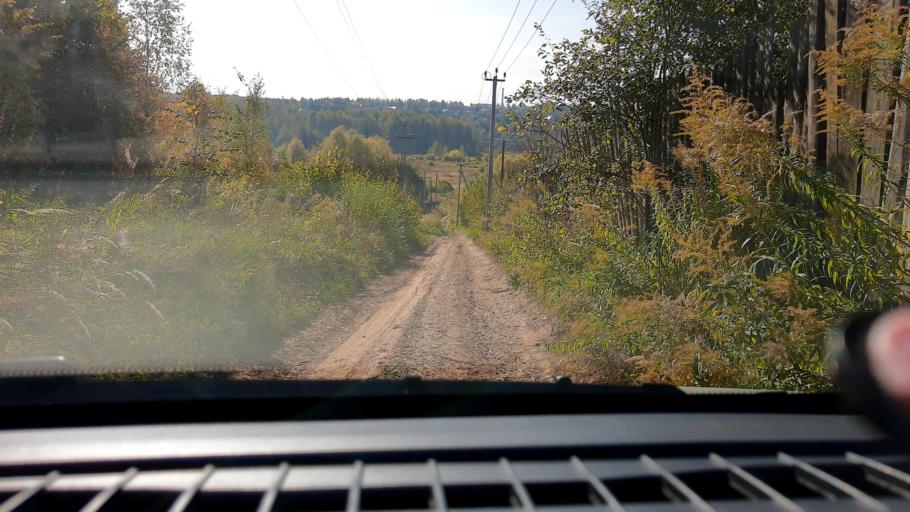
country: RU
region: Nizjnij Novgorod
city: Afonino
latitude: 56.2397
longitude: 44.0591
